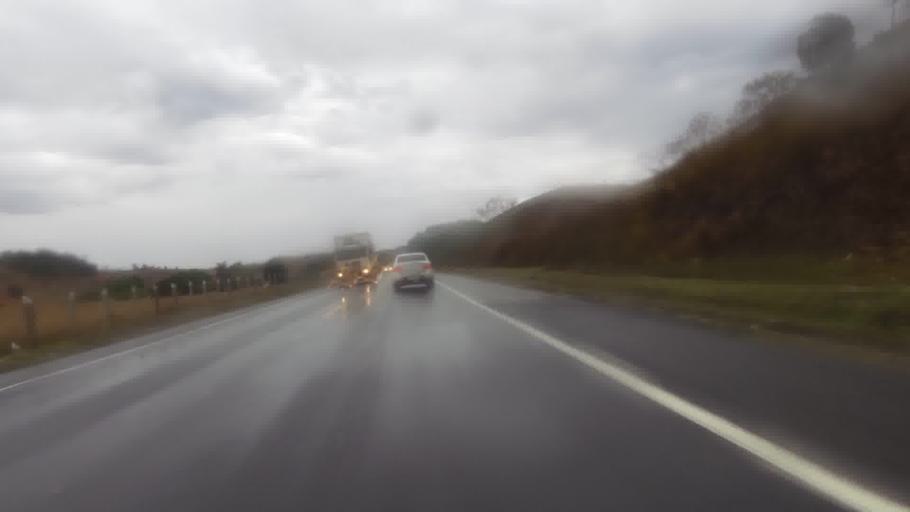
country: BR
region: Espirito Santo
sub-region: Cachoeiro De Itapemirim
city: Cachoeiro de Itapemirim
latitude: -21.0029
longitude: -41.1336
